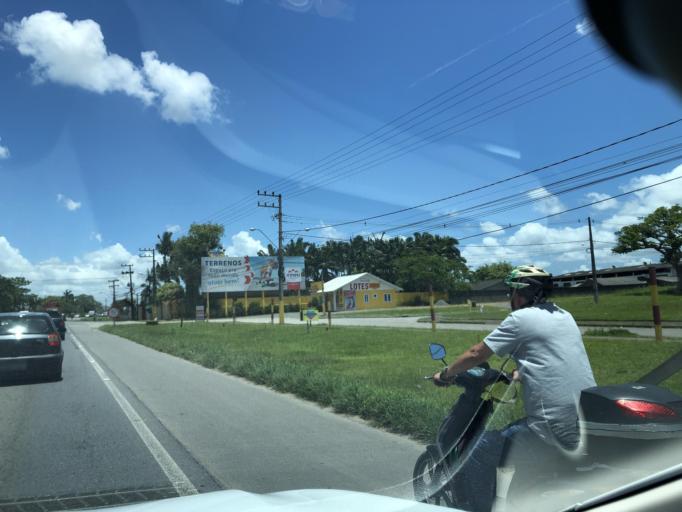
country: BR
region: Santa Catarina
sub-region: Joinville
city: Joinville
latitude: -26.4035
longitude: -48.7449
